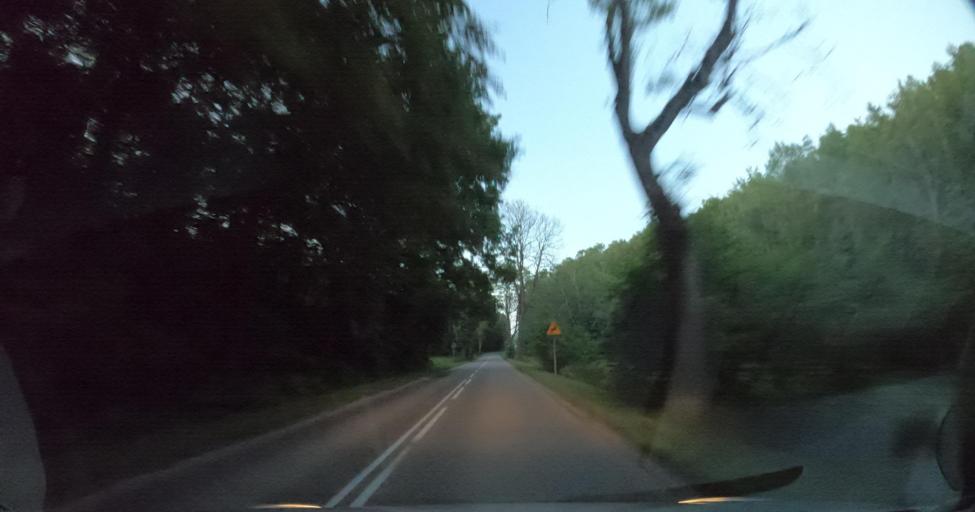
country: PL
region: Pomeranian Voivodeship
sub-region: Powiat wejherowski
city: Koleczkowo
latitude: 54.4676
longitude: 18.2882
